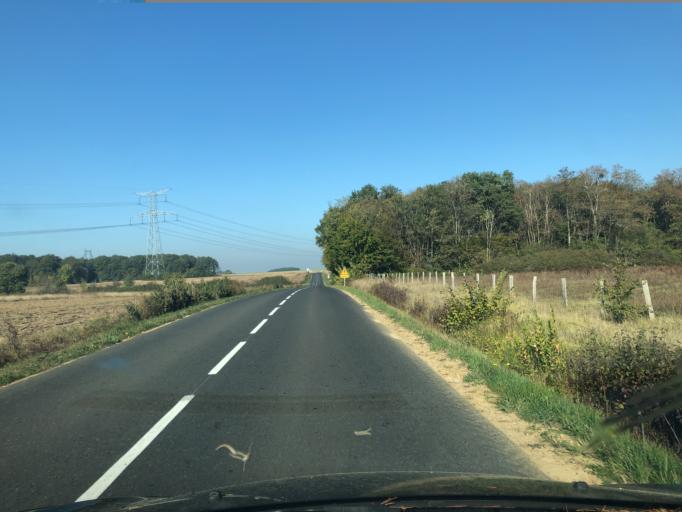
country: FR
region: Centre
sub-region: Departement d'Indre-et-Loire
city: Rouziers-de-Touraine
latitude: 47.5300
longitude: 0.6399
